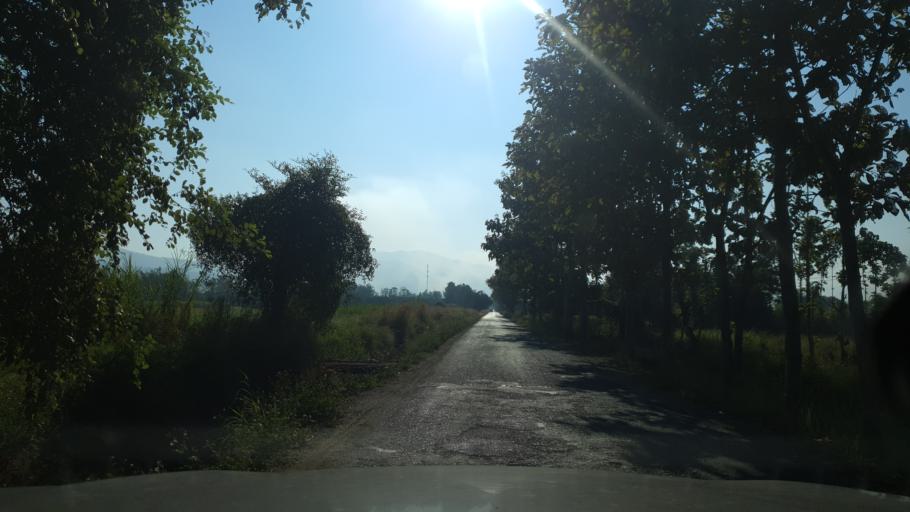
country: TH
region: Chiang Mai
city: San Kamphaeng
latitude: 18.6969
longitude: 99.1489
